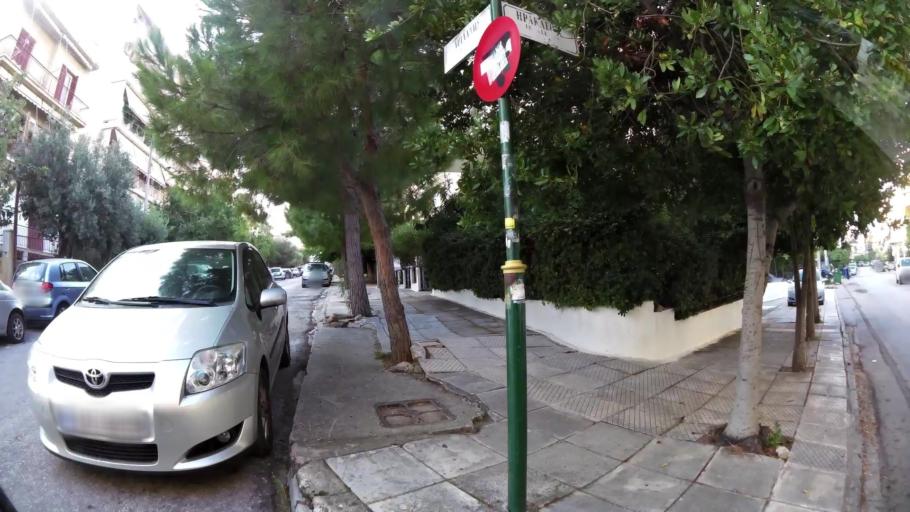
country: GR
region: Attica
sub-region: Nomarchia Athinas
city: Ymittos
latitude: 37.9417
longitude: 23.7523
